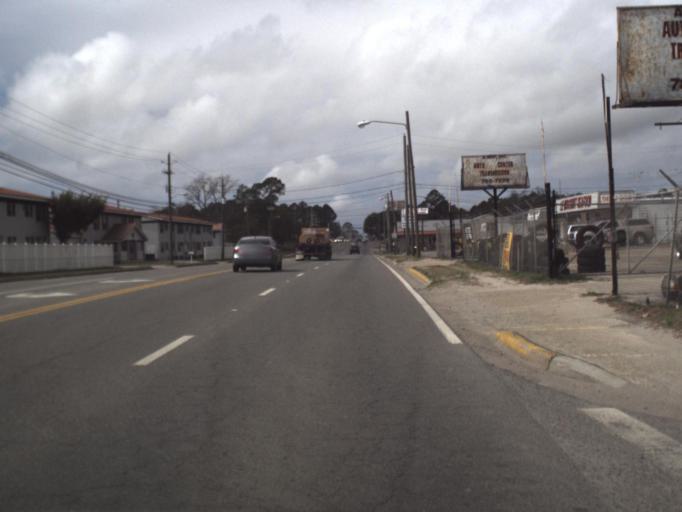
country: US
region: Florida
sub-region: Bay County
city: Panama City
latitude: 30.1751
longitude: -85.6460
